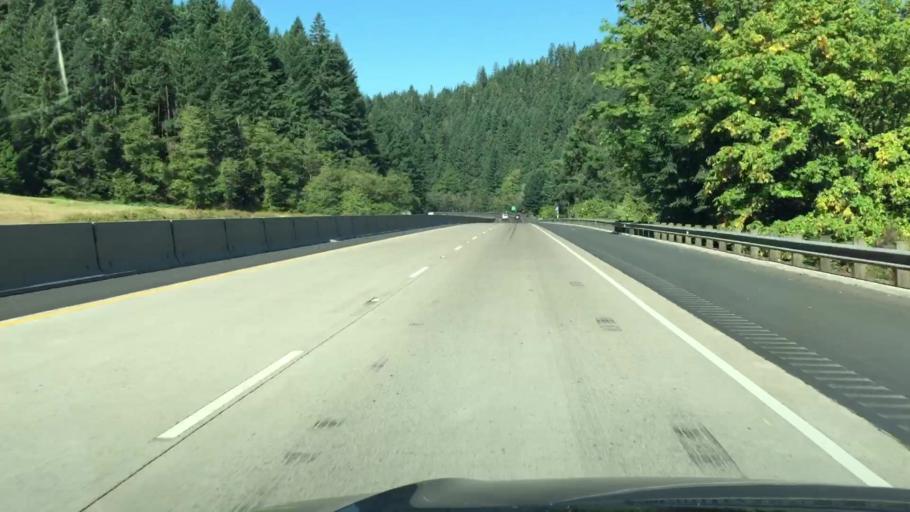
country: US
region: Oregon
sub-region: Lane County
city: Cottage Grove
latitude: 43.7526
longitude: -123.1329
